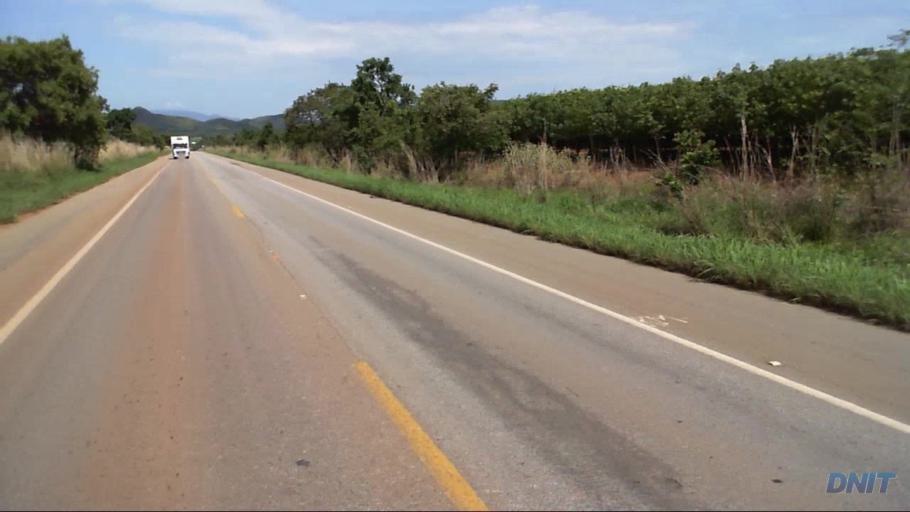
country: BR
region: Goias
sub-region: Barro Alto
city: Barro Alto
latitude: -15.1956
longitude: -48.7667
